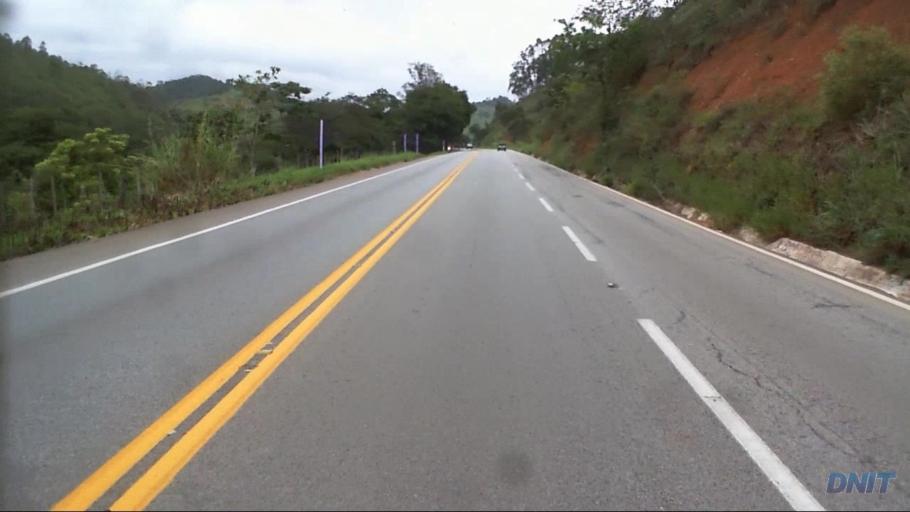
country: BR
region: Minas Gerais
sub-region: Nova Era
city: Nova Era
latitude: -19.7783
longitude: -43.0438
